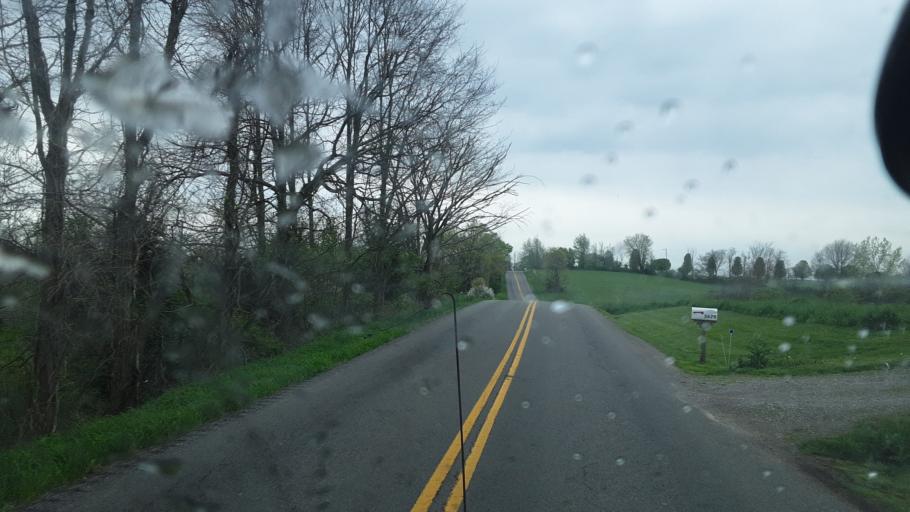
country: US
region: Kentucky
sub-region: Owen County
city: Owenton
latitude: 38.6192
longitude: -84.7866
